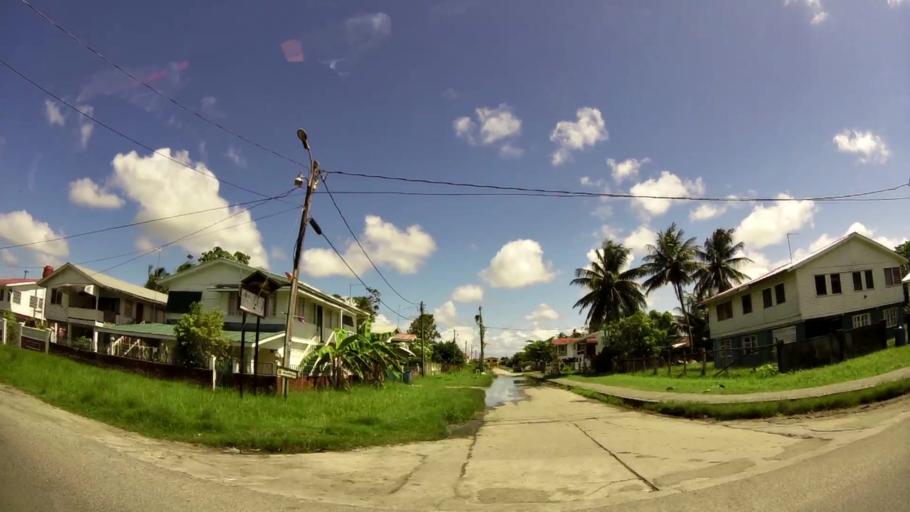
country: GY
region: Demerara-Mahaica
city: Georgetown
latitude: 6.7836
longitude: -58.1303
